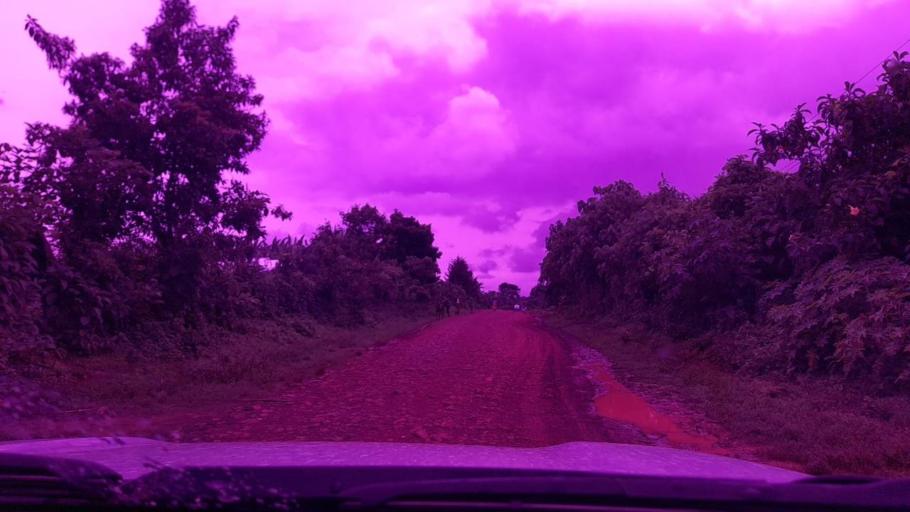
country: ET
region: Southern Nations, Nationalities, and People's Region
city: Tippi
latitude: 7.5741
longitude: 35.6374
